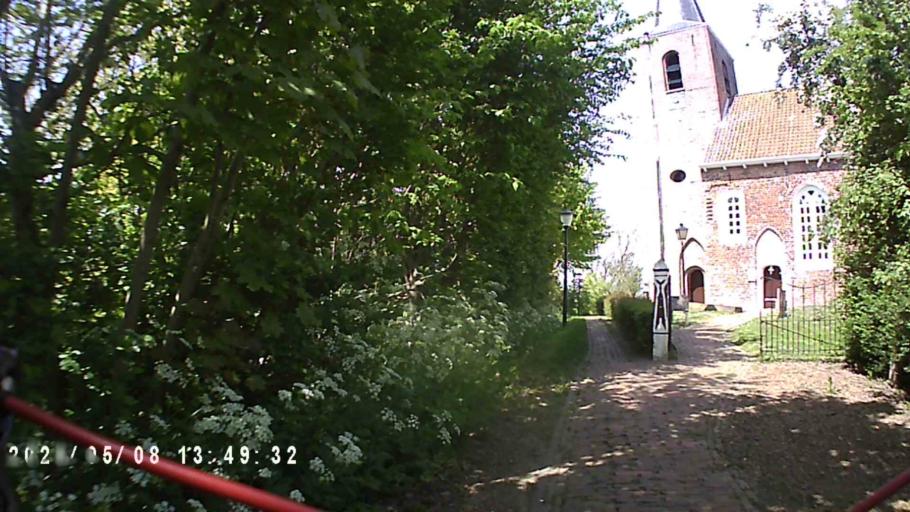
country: NL
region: Groningen
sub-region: Gemeente Appingedam
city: Appingedam
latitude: 53.3394
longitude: 6.7795
